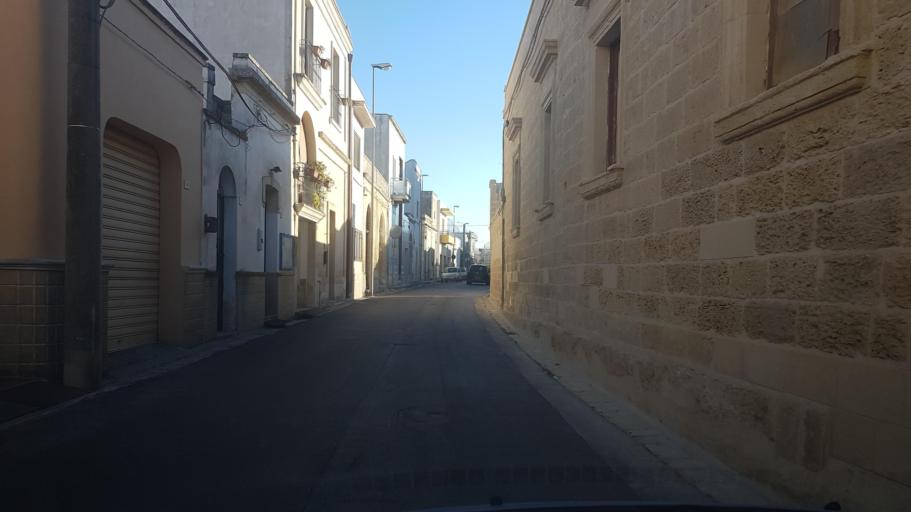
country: IT
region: Apulia
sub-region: Provincia di Lecce
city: Struda
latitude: 40.3217
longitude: 18.2840
